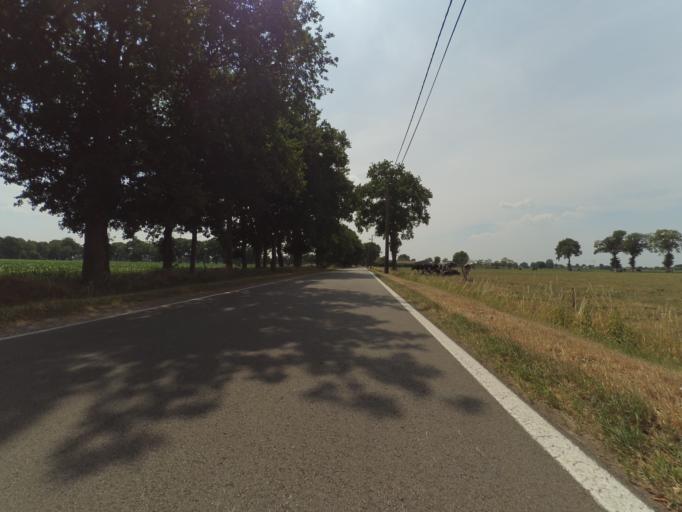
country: BE
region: Flanders
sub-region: Provincie Antwerpen
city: Kalmthout
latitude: 51.4060
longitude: 4.5125
